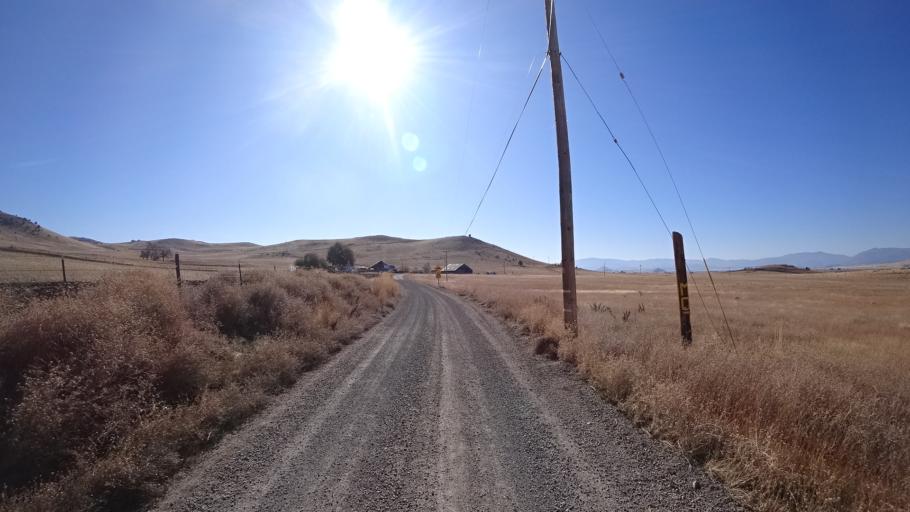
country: US
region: California
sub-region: Siskiyou County
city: Montague
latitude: 41.7968
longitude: -122.4168
